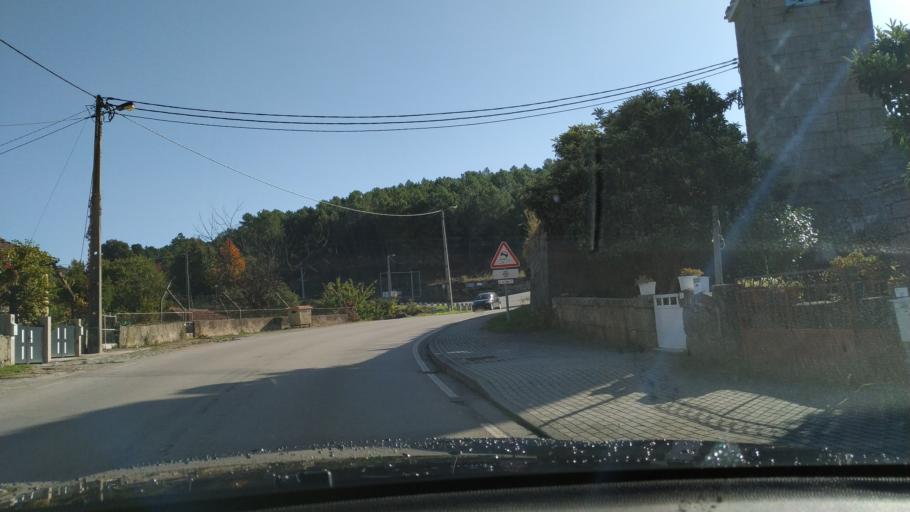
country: PT
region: Vila Real
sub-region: Vila Real
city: Vila Real
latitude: 41.3128
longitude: -7.7170
